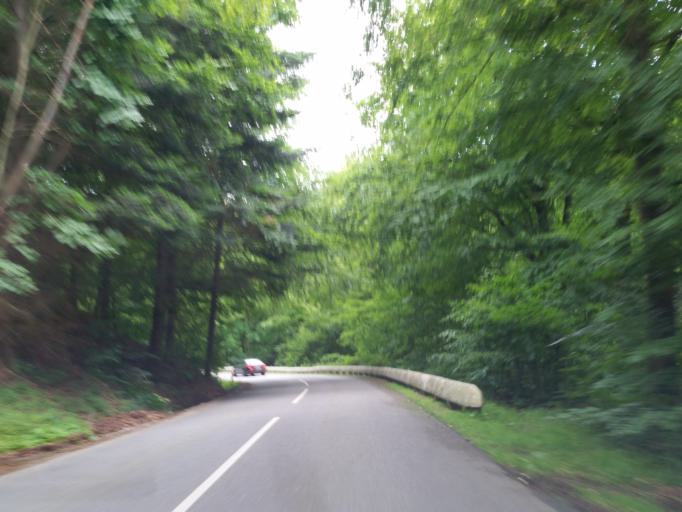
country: DK
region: South Denmark
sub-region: Vejle Kommune
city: Borkop
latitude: 55.6910
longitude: 9.6156
